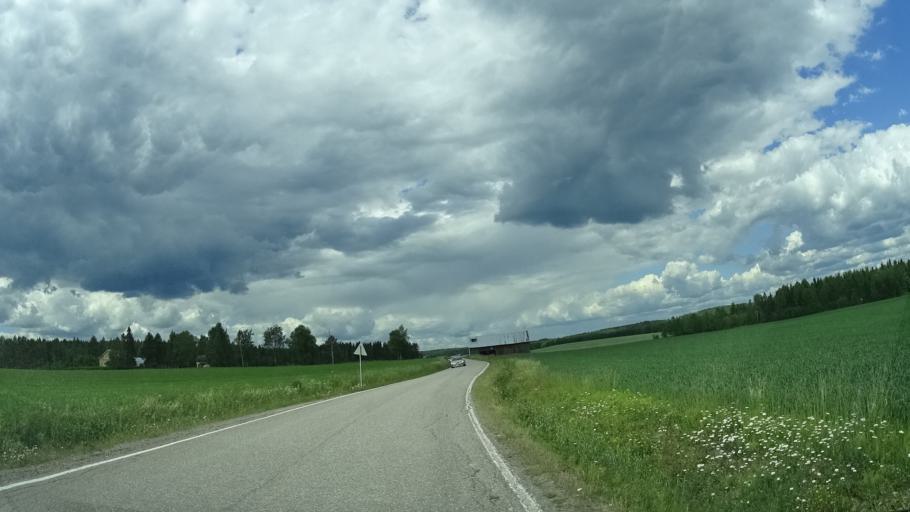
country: FI
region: Uusimaa
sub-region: Helsinki
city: Espoo
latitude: 60.4129
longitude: 24.5565
